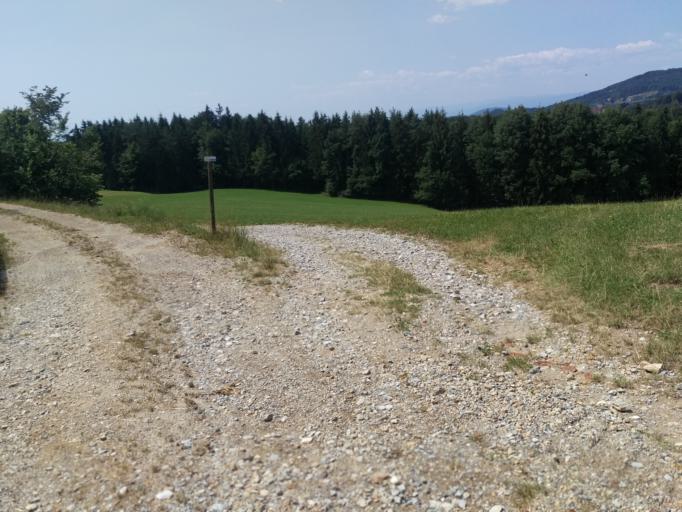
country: AT
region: Styria
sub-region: Graz Stadt
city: Mariatrost
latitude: 47.1251
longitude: 15.5055
